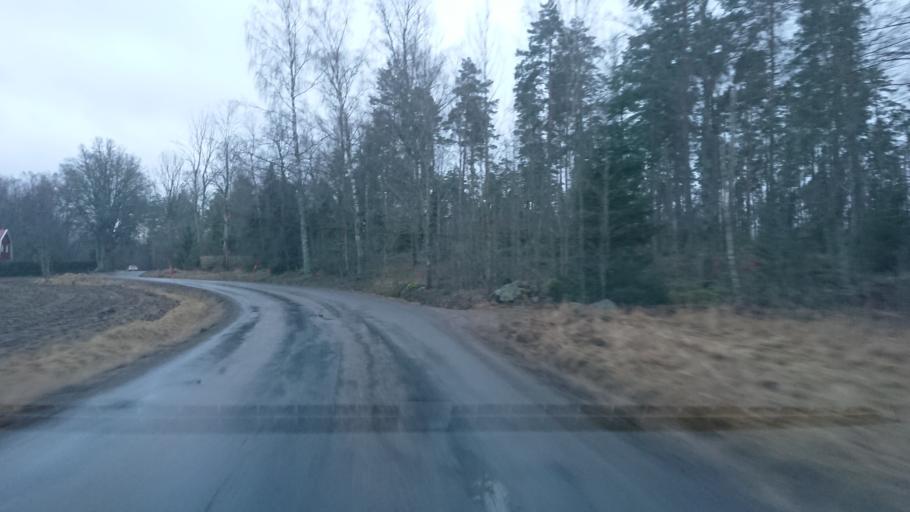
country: SE
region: Uppsala
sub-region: Osthammars Kommun
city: Bjorklinge
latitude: 60.0005
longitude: 17.5941
